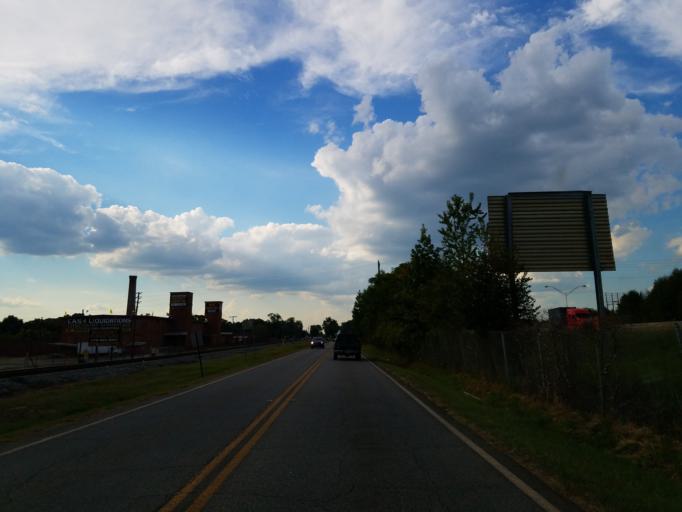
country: US
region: Georgia
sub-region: Monroe County
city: Forsyth
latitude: 33.0507
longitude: -83.9483
